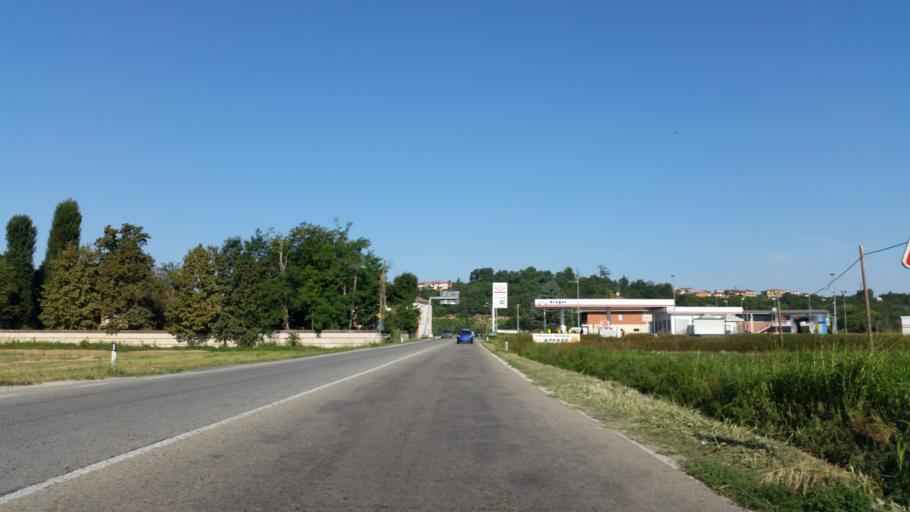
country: IT
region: Piedmont
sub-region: Provincia di Cuneo
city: Roreto
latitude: 44.6667
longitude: 7.8535
